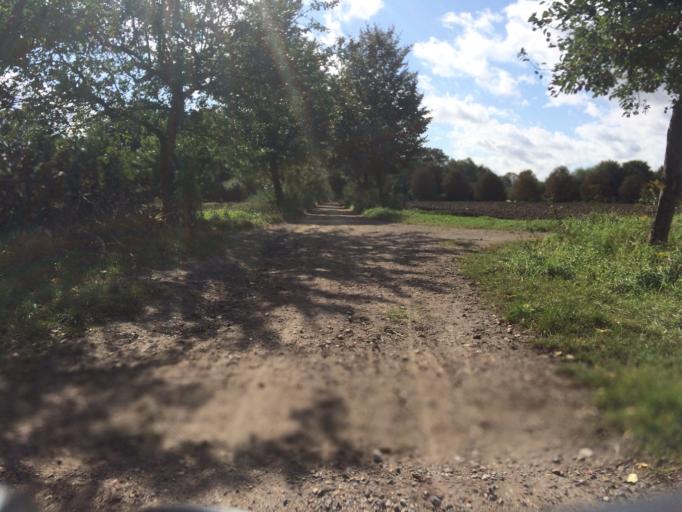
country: DE
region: Berlin
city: Stadtrandsiedlung Malchow
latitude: 52.5808
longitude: 13.4642
